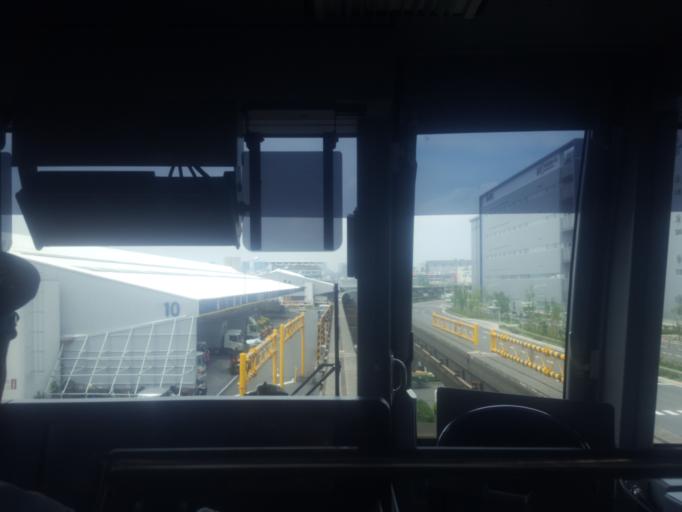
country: JP
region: Kanagawa
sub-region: Kawasaki-shi
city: Kawasaki
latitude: 35.5856
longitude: 139.7474
